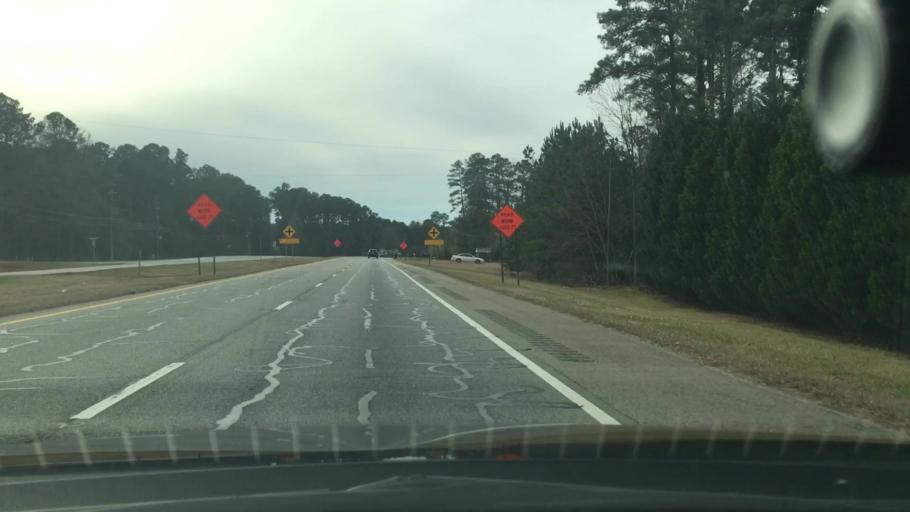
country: US
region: Georgia
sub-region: Fayette County
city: Peachtree City
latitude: 33.4003
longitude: -84.6514
